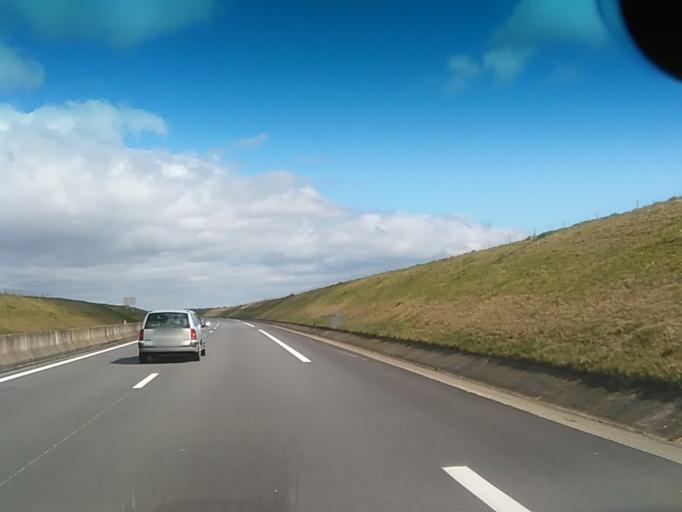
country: FR
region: Lower Normandy
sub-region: Departement du Calvados
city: Orbec
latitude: 49.0536
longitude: 0.4595
